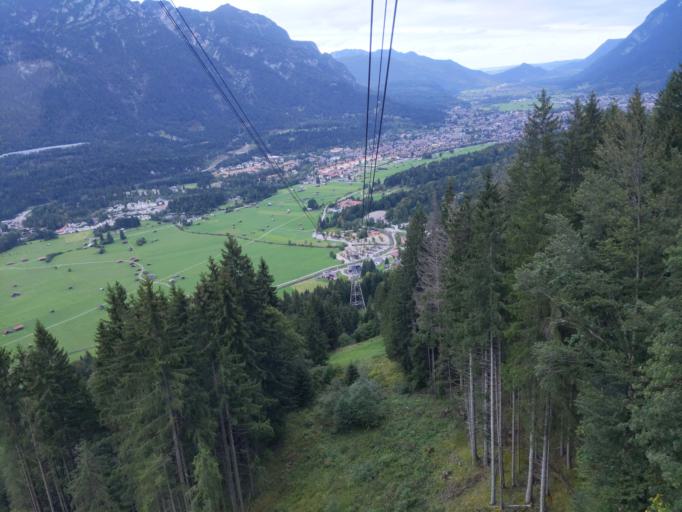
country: DE
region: Bavaria
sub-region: Upper Bavaria
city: Grainau
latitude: 47.4624
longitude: 11.0587
